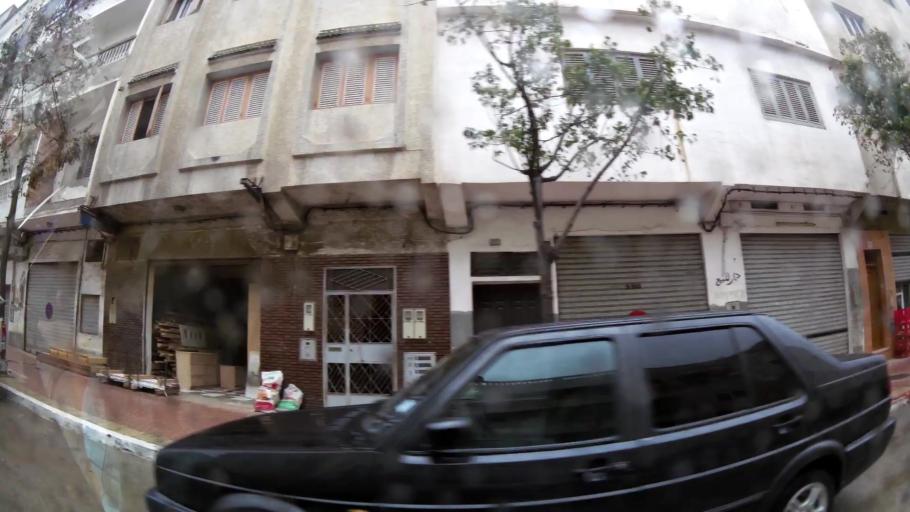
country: MA
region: Taza-Al Hoceima-Taounate
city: Al Hoceima
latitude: 35.2507
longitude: -3.9380
